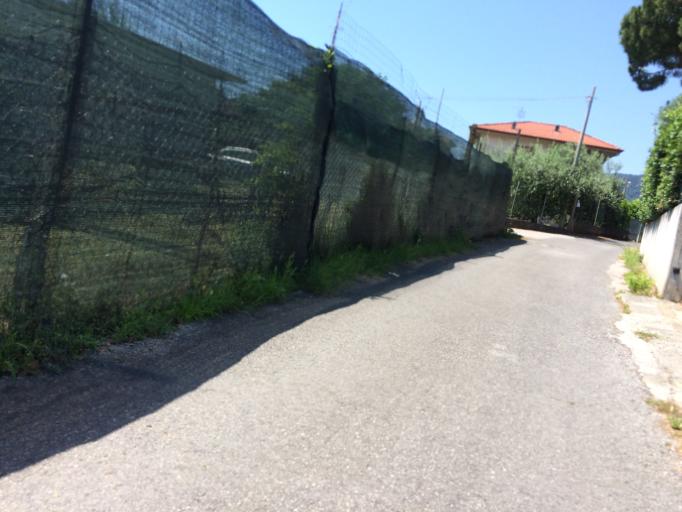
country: IT
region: Tuscany
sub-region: Provincia di Massa-Carrara
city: Massa
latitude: 44.0371
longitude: 10.1290
